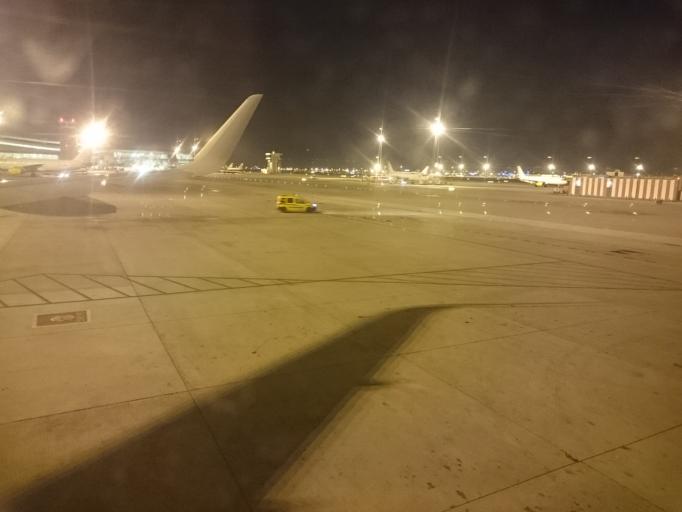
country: ES
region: Catalonia
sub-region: Provincia de Barcelona
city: El Prat de Llobregat
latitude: 41.2924
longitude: 2.0815
